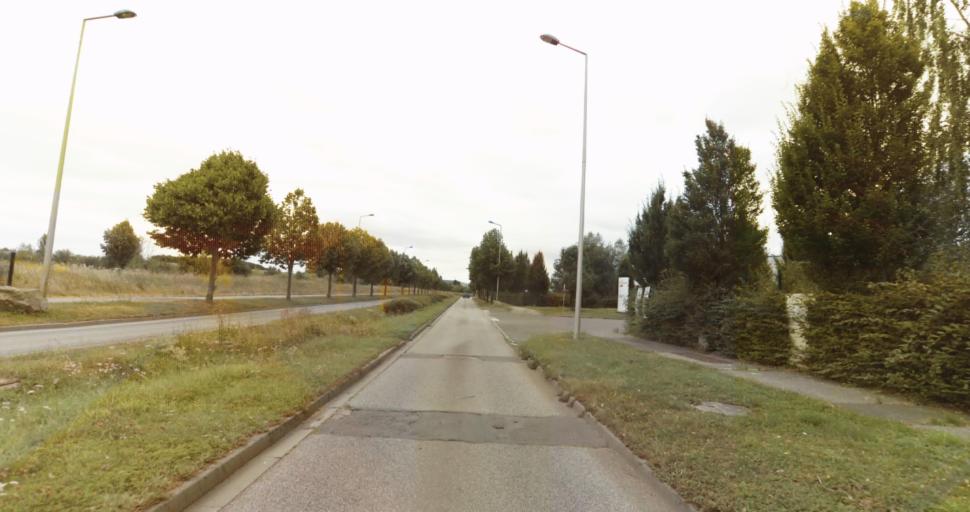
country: FR
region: Haute-Normandie
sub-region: Departement de l'Eure
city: Evreux
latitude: 49.0121
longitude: 1.1857
